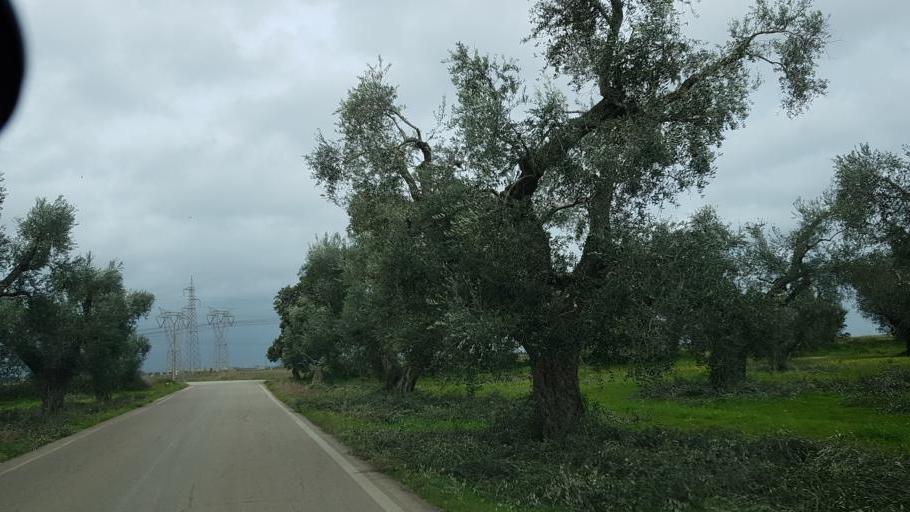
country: IT
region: Apulia
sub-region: Provincia di Brindisi
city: Brindisi
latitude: 40.5984
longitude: 17.8983
